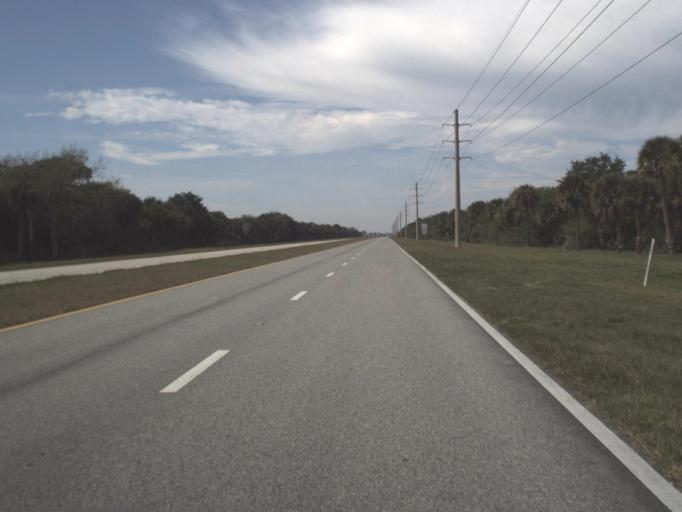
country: US
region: Florida
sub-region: Brevard County
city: Merritt Island
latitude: 28.5265
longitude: -80.7126
